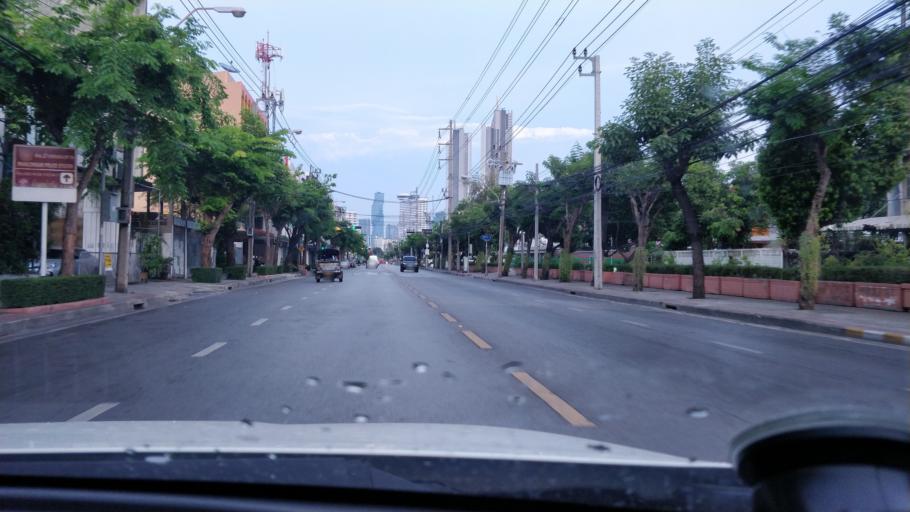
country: TH
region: Bangkok
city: Khlong San
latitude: 13.7334
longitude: 100.4992
